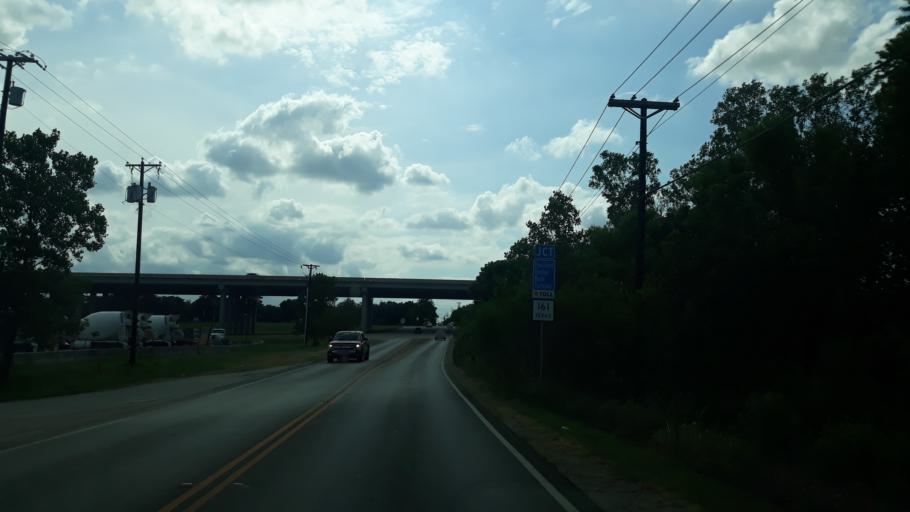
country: US
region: Texas
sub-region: Dallas County
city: Irving
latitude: 32.8159
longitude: -97.0158
